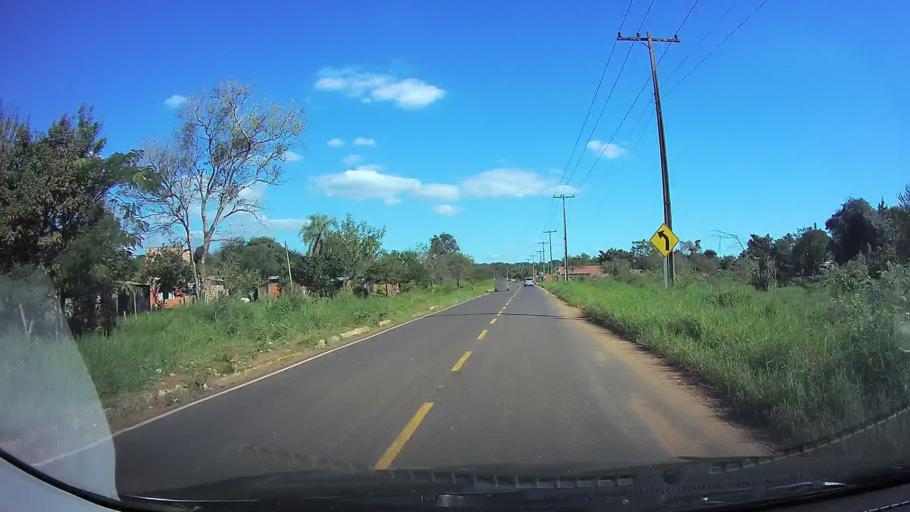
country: PY
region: Central
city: Limpio
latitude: -25.1902
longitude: -57.4750
